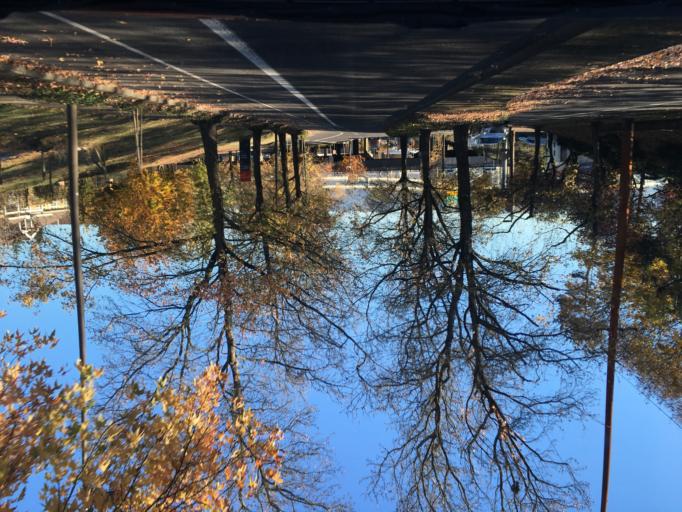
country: US
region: Oregon
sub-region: Multnomah County
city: Portland
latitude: 45.5410
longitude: -122.6697
